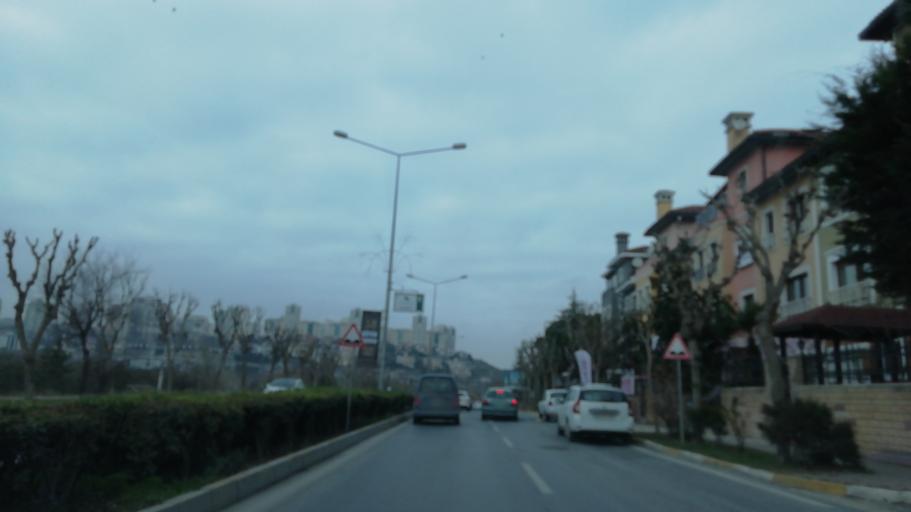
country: TR
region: Istanbul
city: Esenyurt
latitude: 41.0673
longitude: 28.6964
